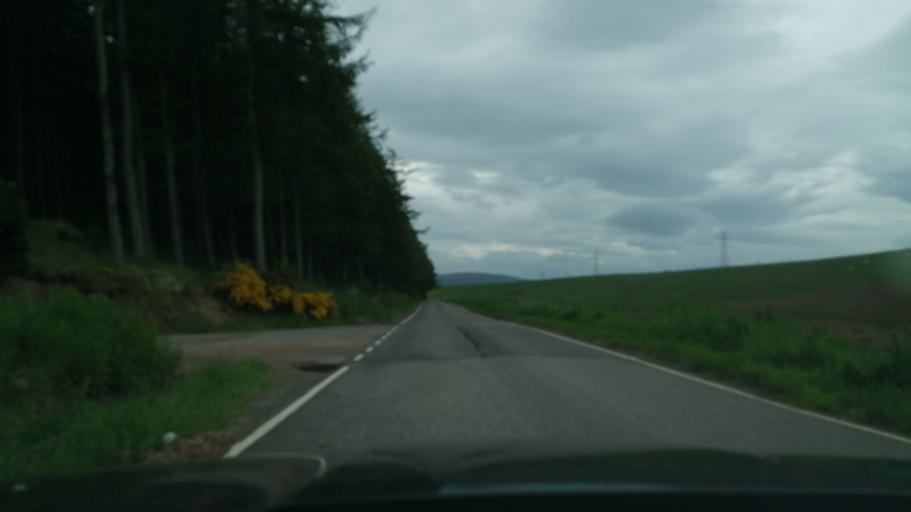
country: GB
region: Scotland
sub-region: Moray
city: Cullen
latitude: 57.5995
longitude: -2.8546
